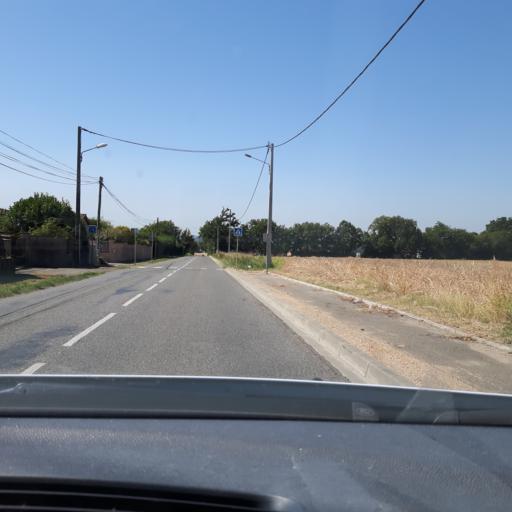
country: FR
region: Midi-Pyrenees
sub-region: Departement de la Haute-Garonne
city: Bouloc
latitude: 43.7746
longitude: 1.3923
